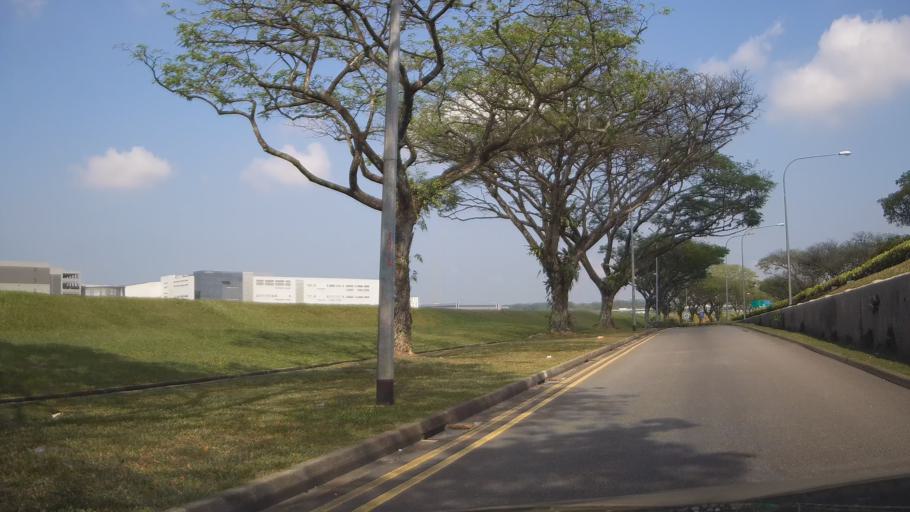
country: MY
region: Johor
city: Johor Bahru
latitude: 1.3561
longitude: 103.7162
